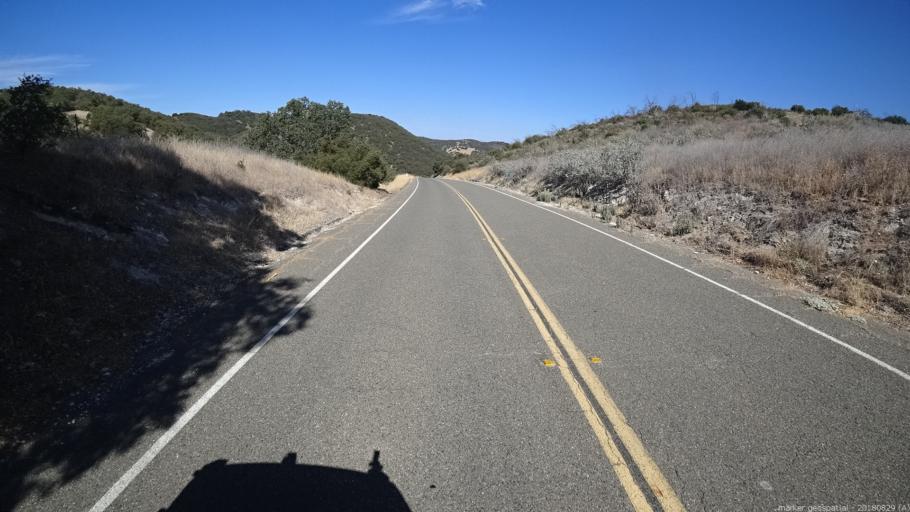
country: US
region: California
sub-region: San Luis Obispo County
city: Lake Nacimiento
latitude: 35.8505
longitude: -121.0521
